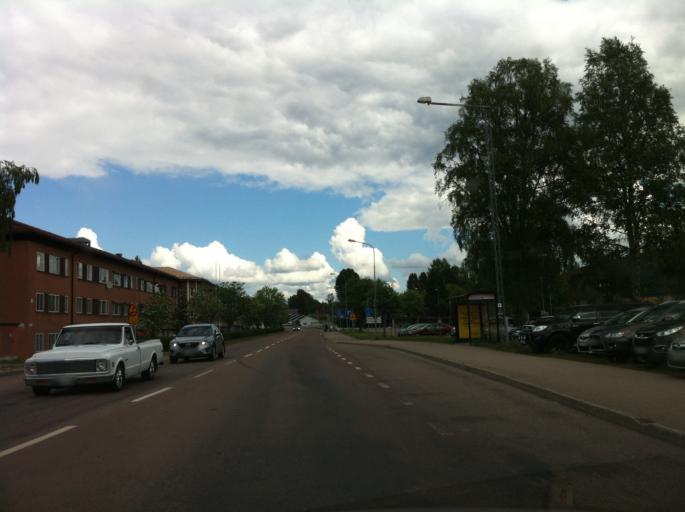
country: SE
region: Dalarna
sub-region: Malung-Saelens kommun
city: Malung
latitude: 60.6846
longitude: 13.7185
